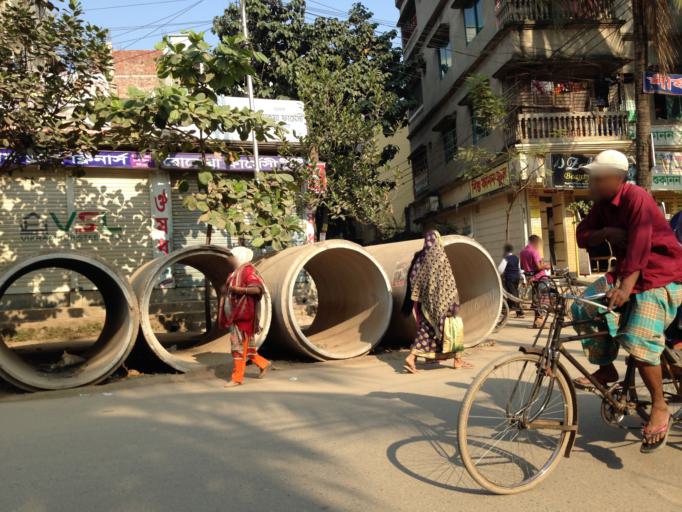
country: BD
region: Dhaka
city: Azimpur
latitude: 23.8023
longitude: 90.3489
